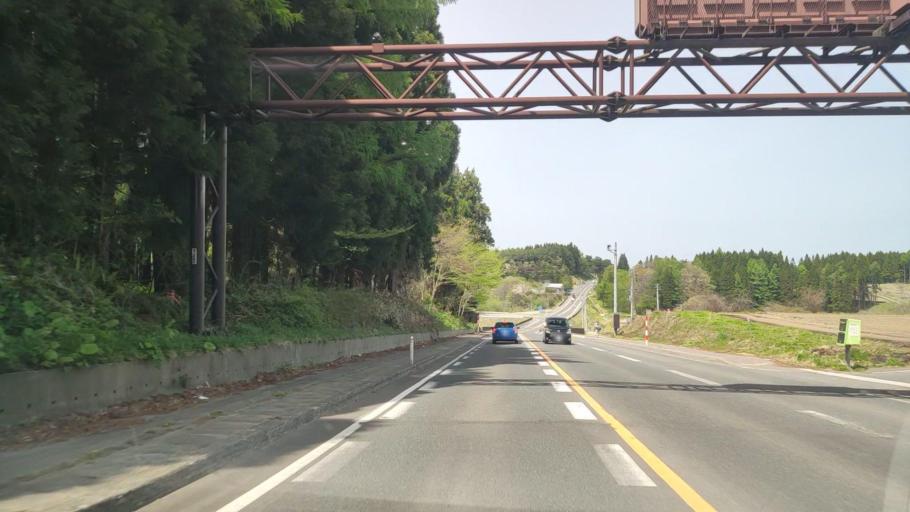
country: JP
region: Aomori
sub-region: Misawa Shi
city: Inuotose
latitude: 40.6618
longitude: 141.1892
